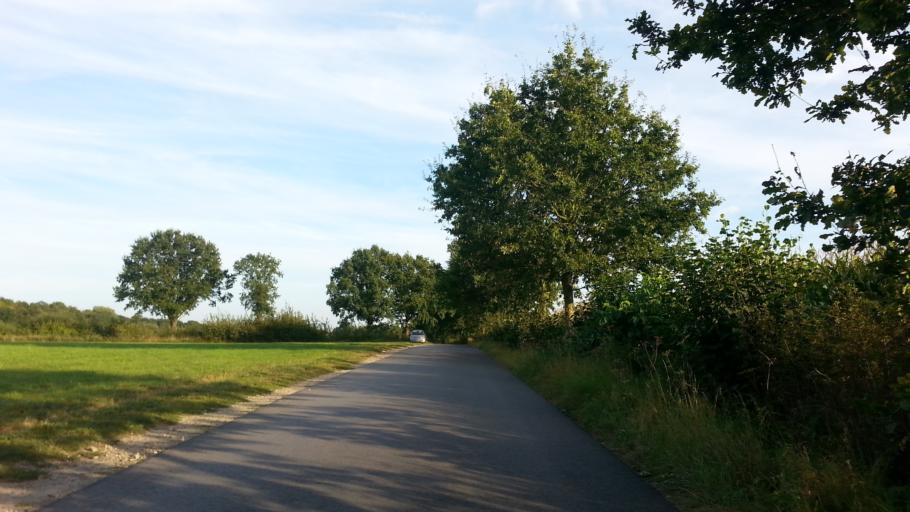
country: DE
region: North Rhine-Westphalia
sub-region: Regierungsbezirk Munster
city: Muenster
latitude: 51.9452
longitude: 7.5783
